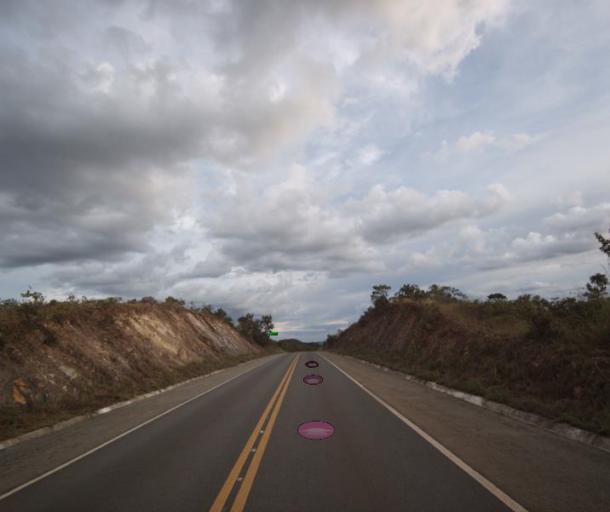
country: BR
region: Goias
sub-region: Barro Alto
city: Barro Alto
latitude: -14.9046
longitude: -48.6444
